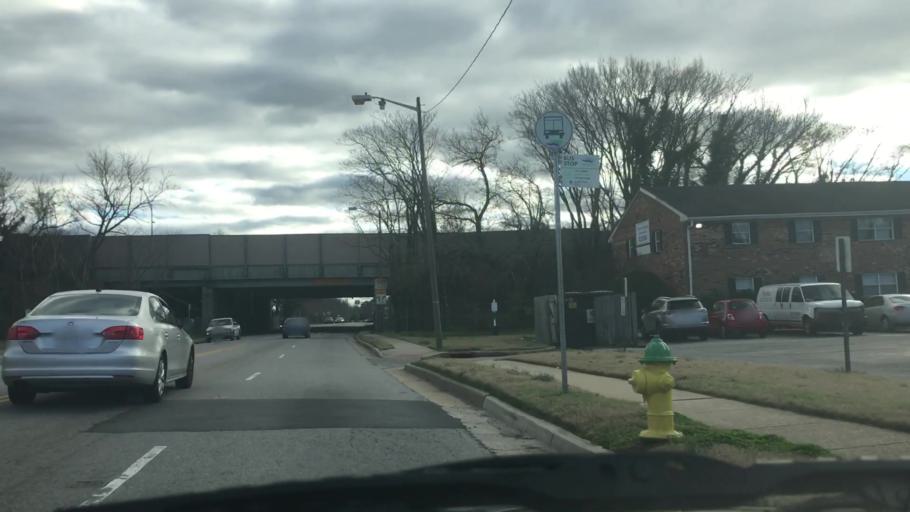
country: US
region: Virginia
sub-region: City of Norfolk
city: Norfolk
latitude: 36.9043
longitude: -76.2430
